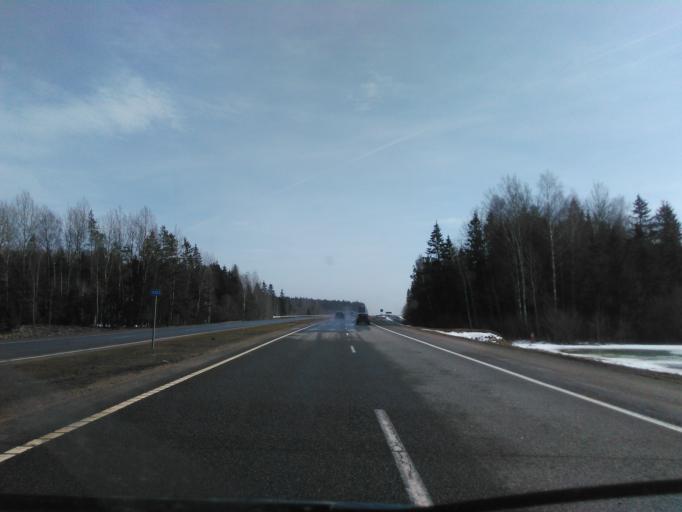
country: BY
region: Vitebsk
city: Kokhanava
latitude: 54.4789
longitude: 29.8417
